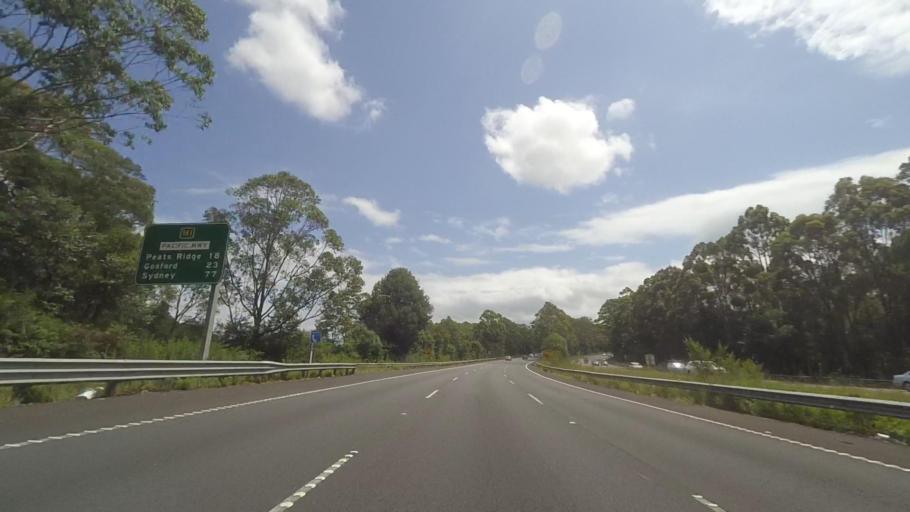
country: AU
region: New South Wales
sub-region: Gosford Shire
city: Lisarow
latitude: -33.3502
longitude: 151.3639
